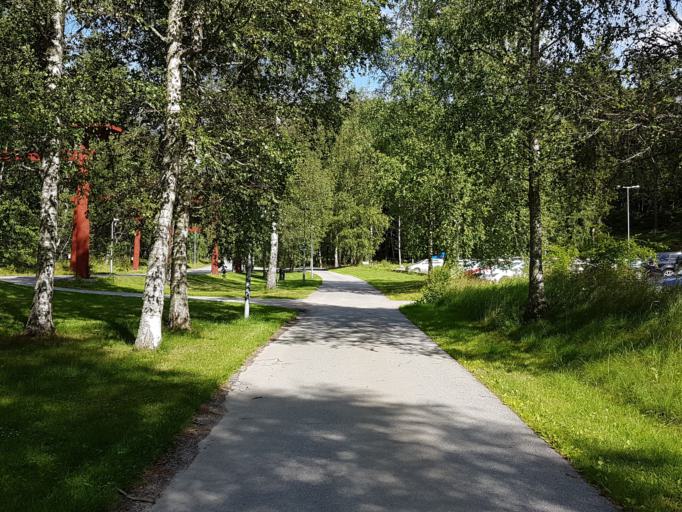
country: SE
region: Stockholm
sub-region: Lidingo
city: Brevik
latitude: 59.3441
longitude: 18.2407
